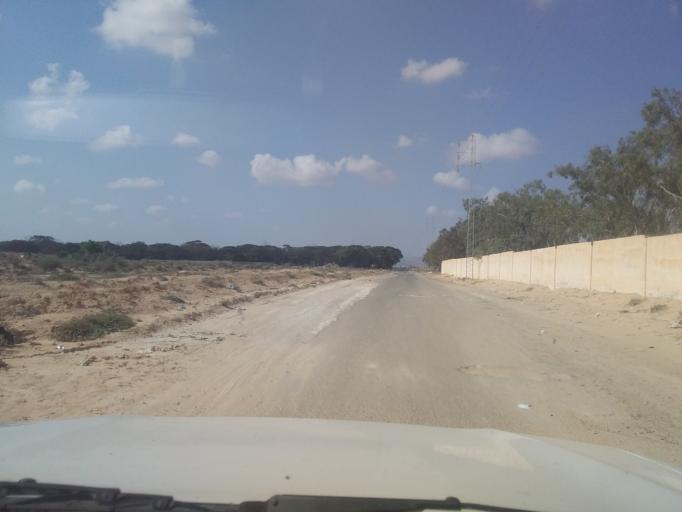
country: TN
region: Qabis
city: Gabes
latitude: 33.6310
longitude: 10.2735
